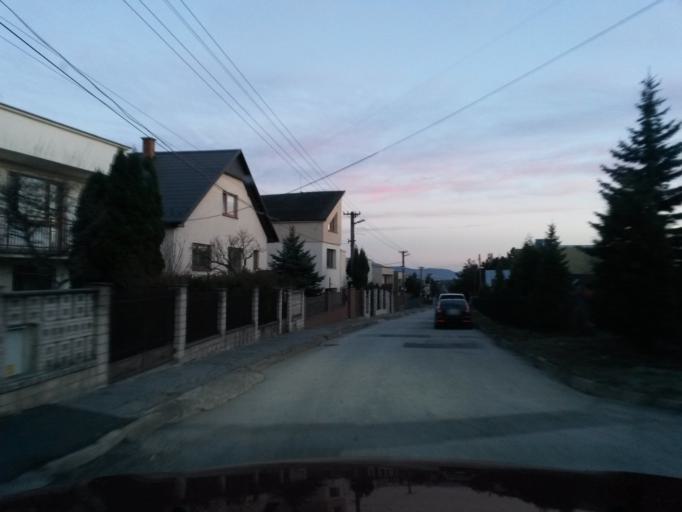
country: SK
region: Kosicky
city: Kosice
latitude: 48.7369
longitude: 21.2932
